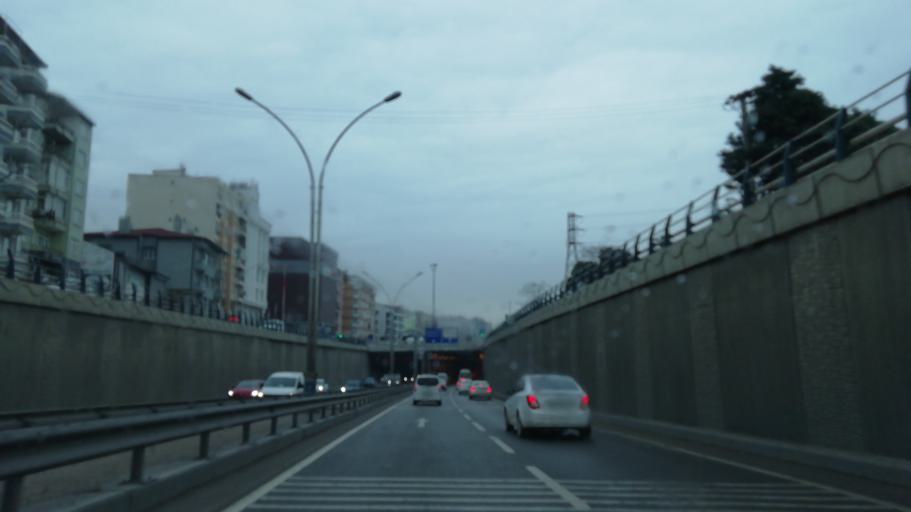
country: TR
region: Kocaeli
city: Izmit
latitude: 40.7662
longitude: 29.9079
